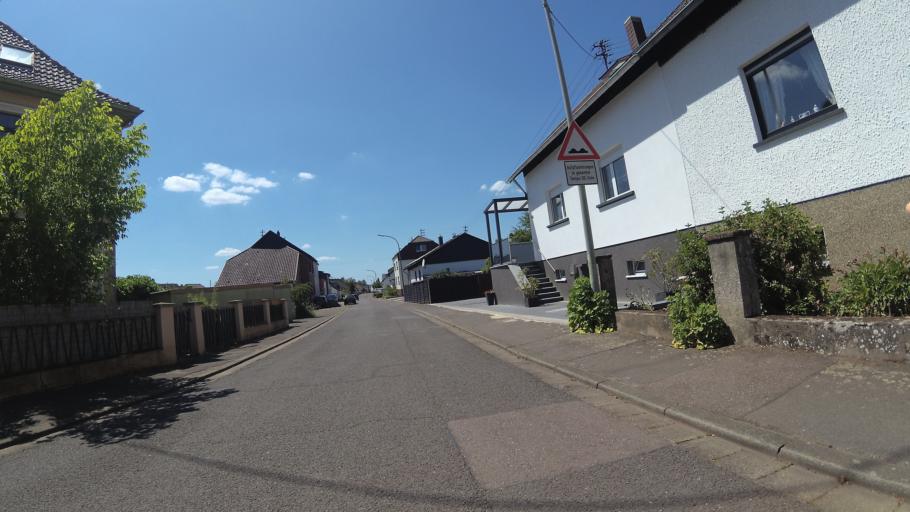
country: DE
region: Saarland
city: Saarwellingen
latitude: 49.3597
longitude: 6.8103
